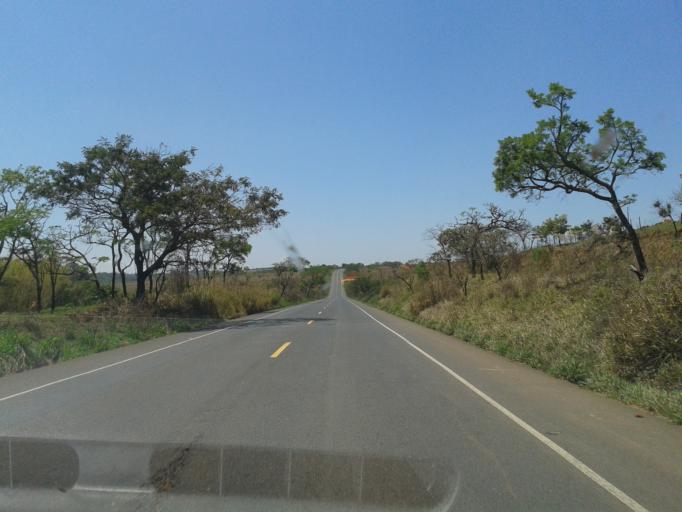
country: BR
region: Minas Gerais
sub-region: Araxa
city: Araxa
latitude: -19.4745
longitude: -47.1544
